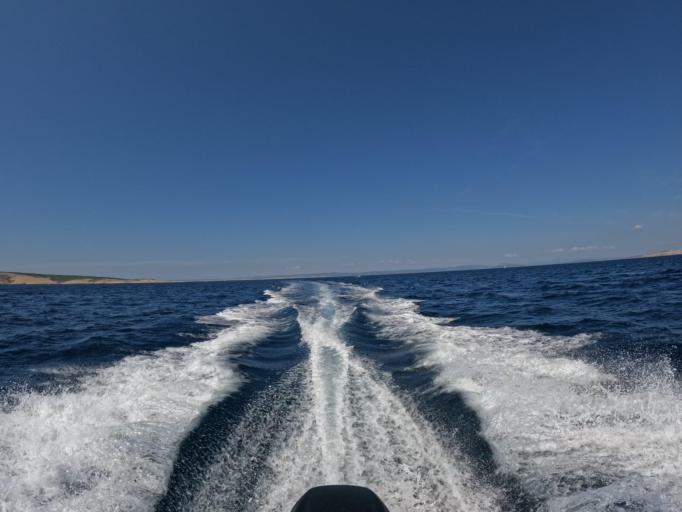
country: HR
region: Primorsko-Goranska
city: Lopar
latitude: 44.8540
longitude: 14.7152
